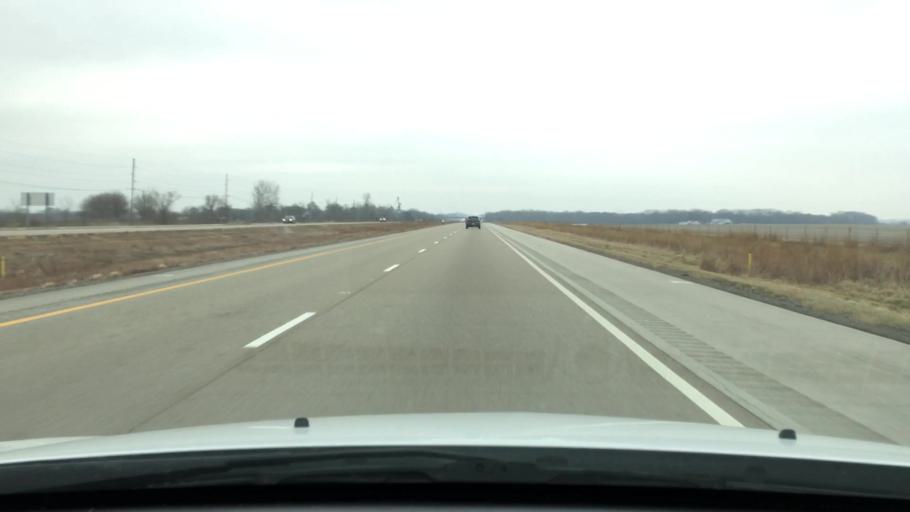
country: US
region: Illinois
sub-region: Logan County
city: Atlanta
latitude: 40.2076
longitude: -89.2927
